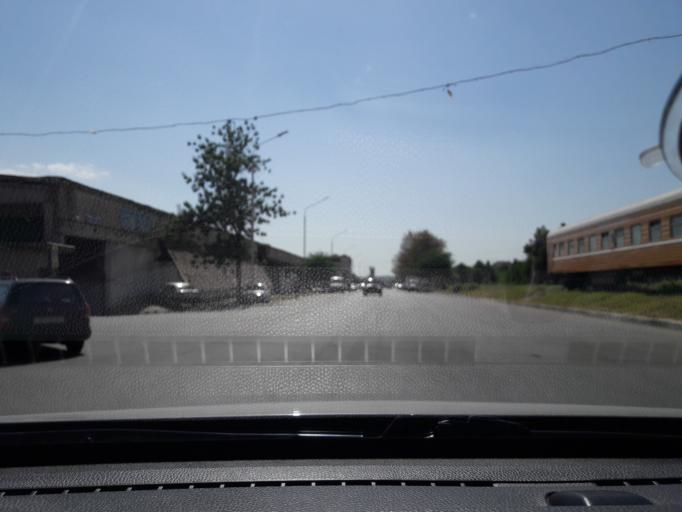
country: TJ
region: Dushanbe
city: Dushanbe
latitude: 38.5676
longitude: 68.7406
